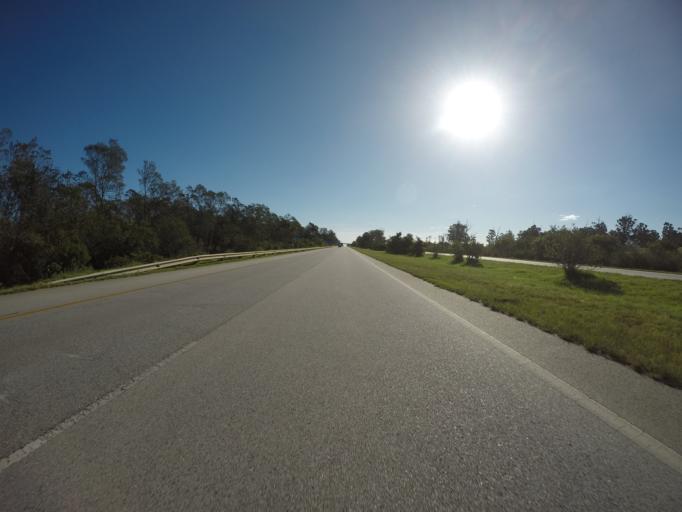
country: ZA
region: Eastern Cape
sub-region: Nelson Mandela Bay Metropolitan Municipality
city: Uitenhage
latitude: -33.9021
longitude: 25.1779
